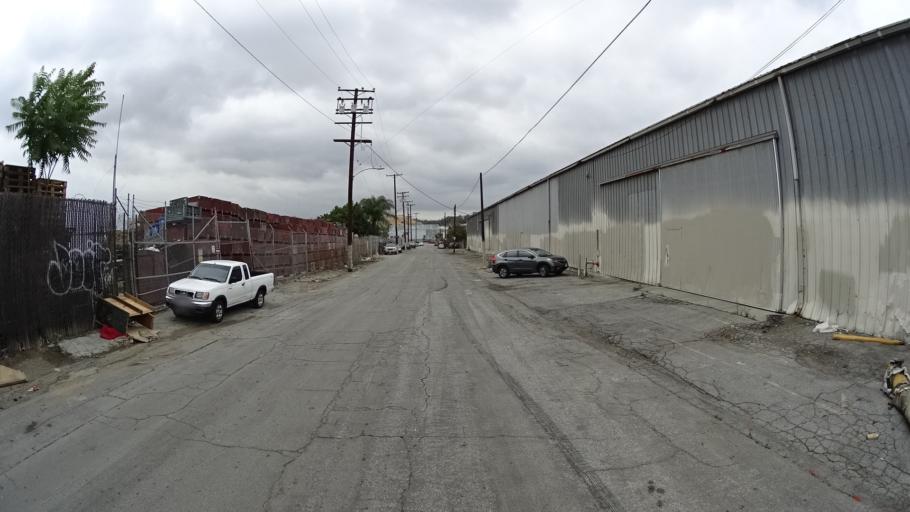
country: US
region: California
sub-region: Los Angeles County
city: Belvedere
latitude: 34.0585
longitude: -118.1892
